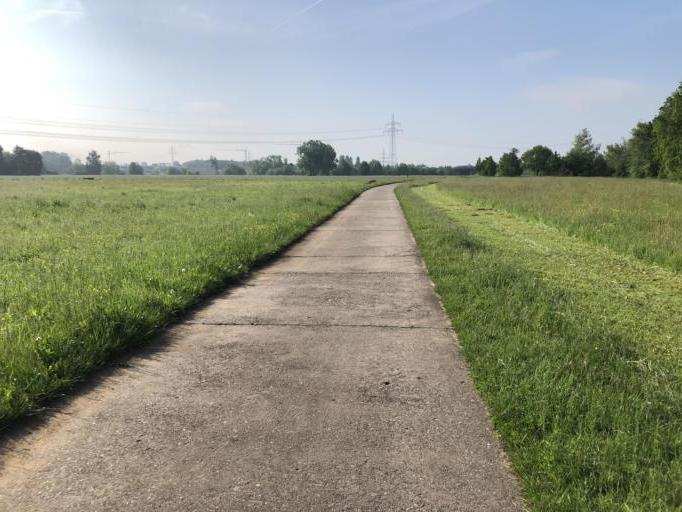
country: DE
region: Bavaria
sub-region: Regierungsbezirk Mittelfranken
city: Erlangen
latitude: 49.5651
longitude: 10.9782
